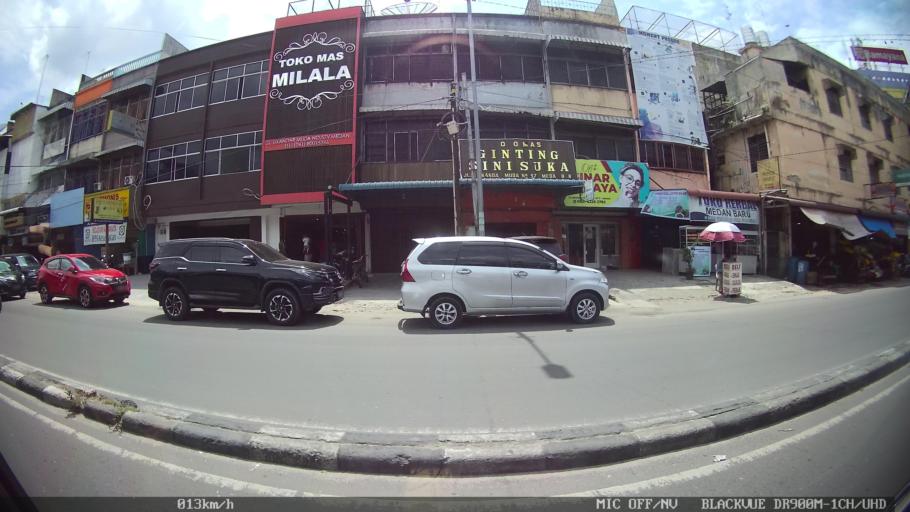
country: ID
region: North Sumatra
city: Medan
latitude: 3.5800
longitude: 98.6611
